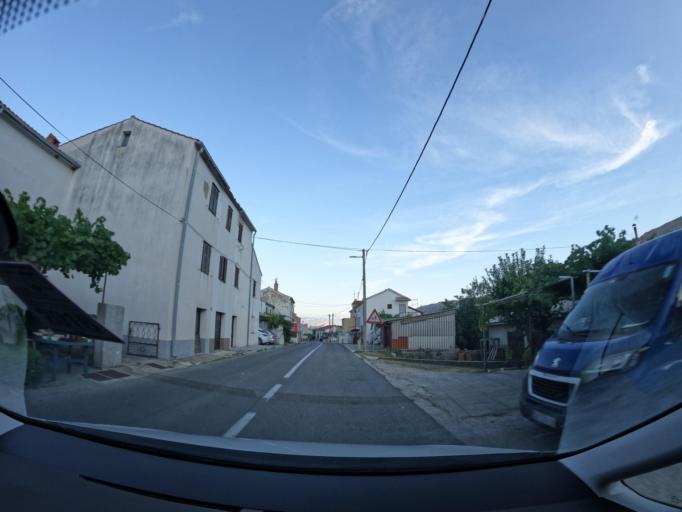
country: HR
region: Primorsko-Goranska
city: Punat
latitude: 44.9964
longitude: 14.7134
